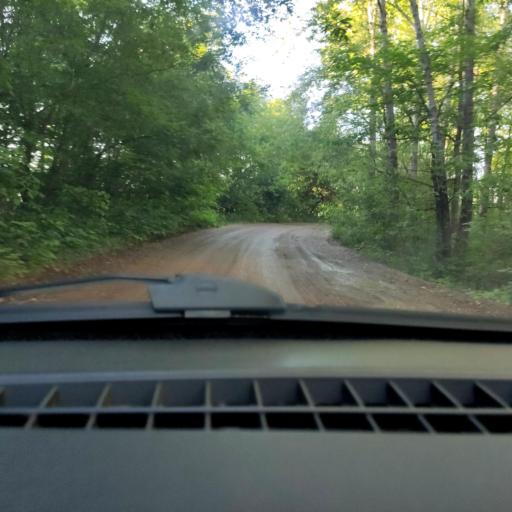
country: RU
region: Bashkortostan
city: Avdon
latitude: 54.6083
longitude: 55.6721
